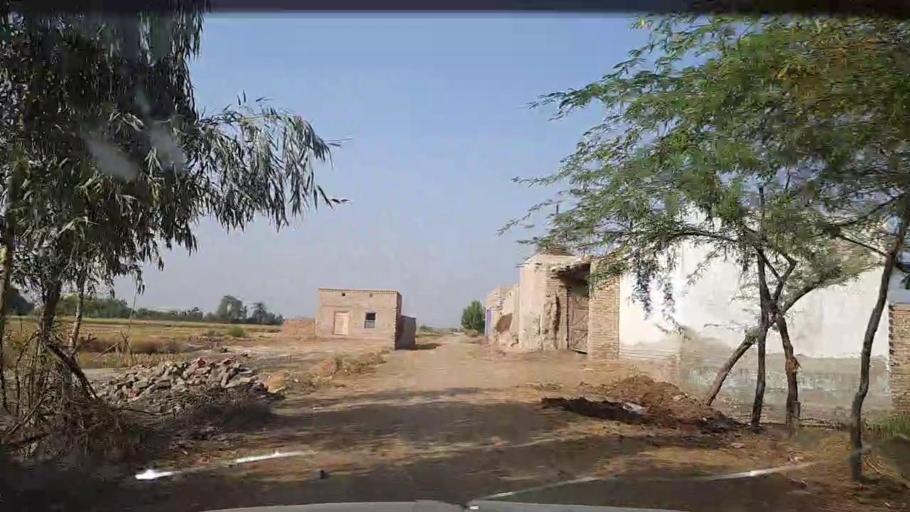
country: PK
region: Sindh
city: Shikarpur
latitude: 28.1218
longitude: 68.5786
